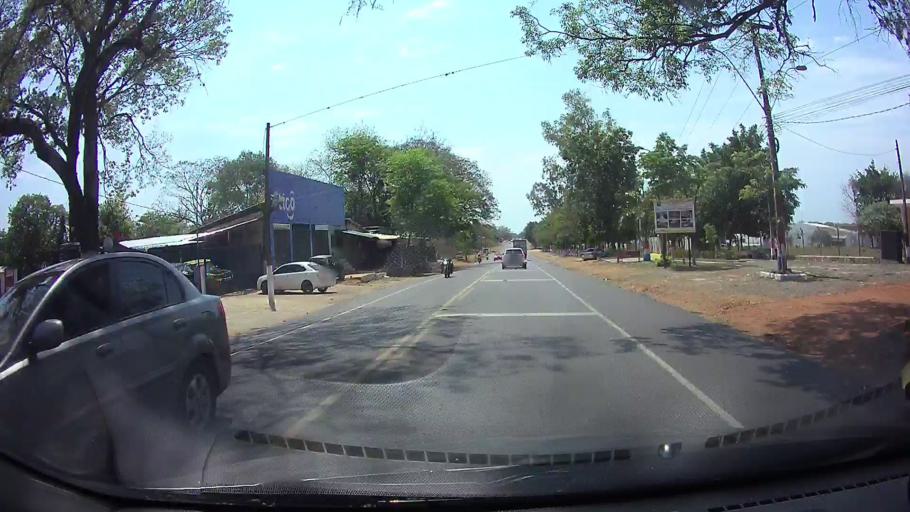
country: PY
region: Central
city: Capiata
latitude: -25.4067
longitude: -57.4615
